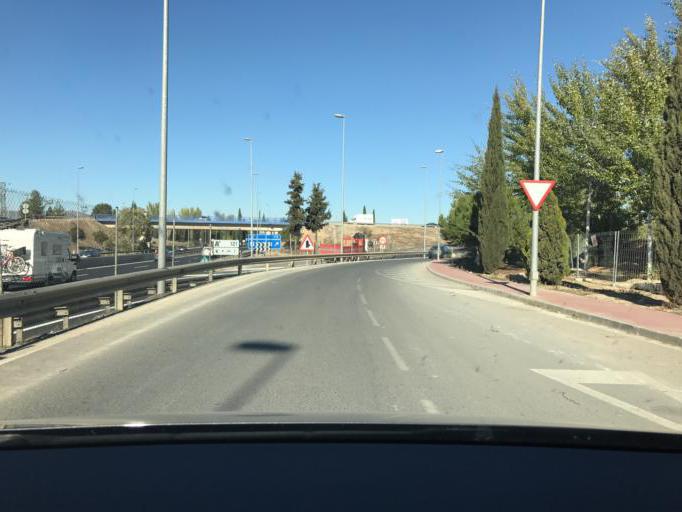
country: ES
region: Andalusia
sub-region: Provincia de Granada
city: Peligros
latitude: 37.2278
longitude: -3.6363
